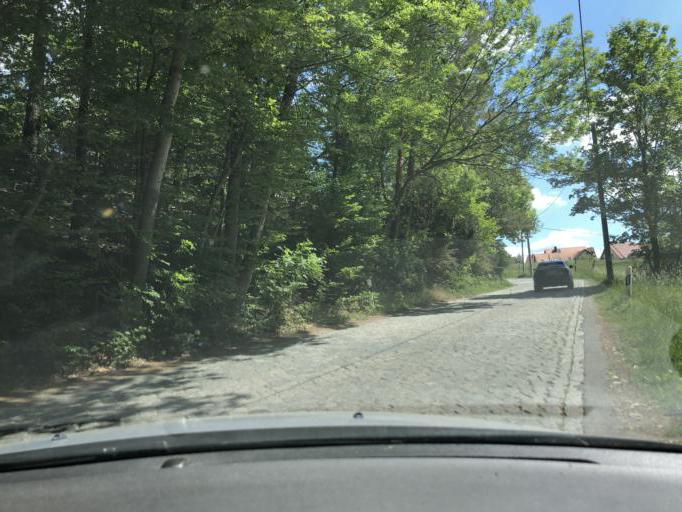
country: DE
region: Saxony
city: Radebeul
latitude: 51.0591
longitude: 13.6456
